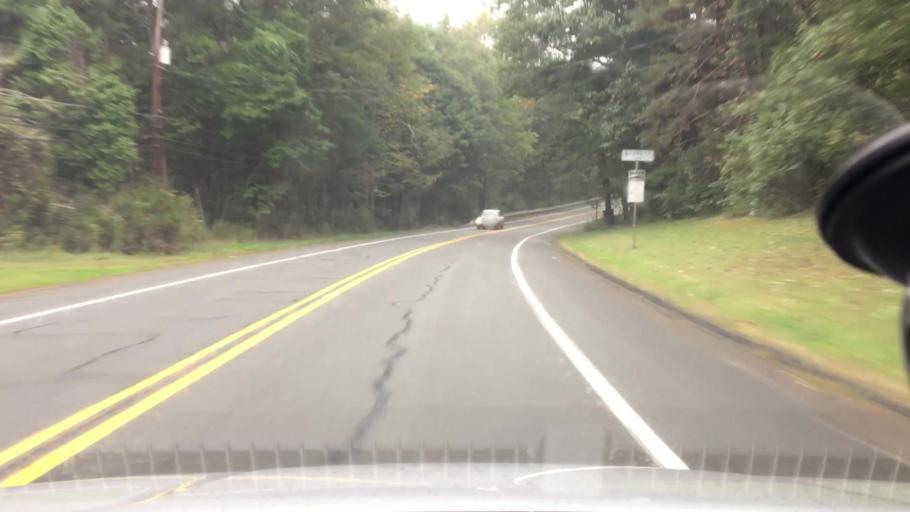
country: US
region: Pennsylvania
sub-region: Monroe County
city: Mountainhome
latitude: 41.1456
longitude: -75.2898
